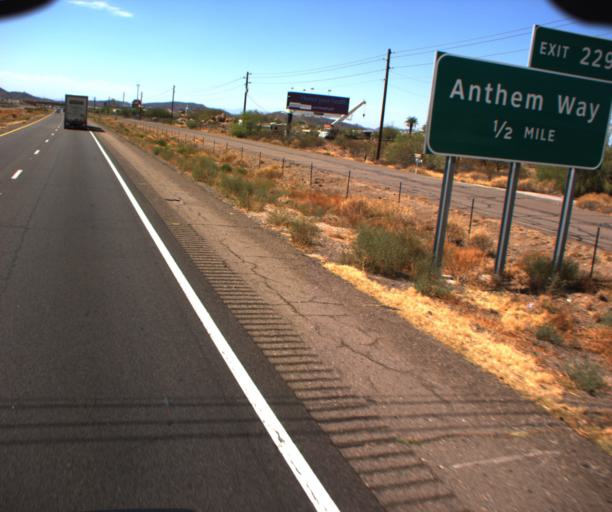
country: US
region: Arizona
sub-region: Maricopa County
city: Anthem
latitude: 33.8822
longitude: -112.1476
